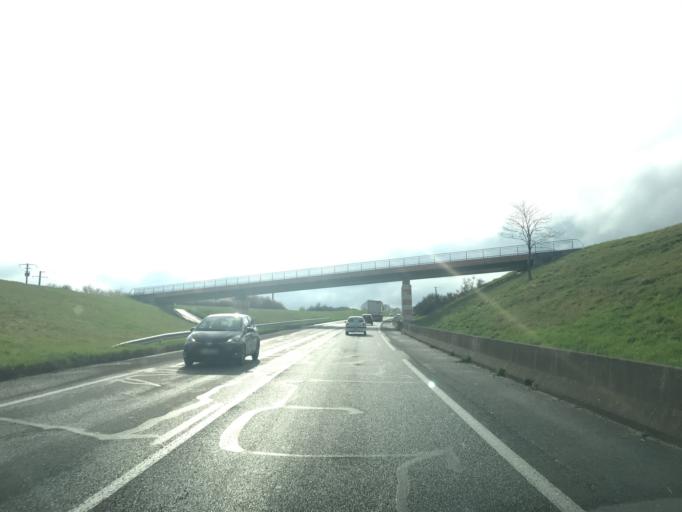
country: FR
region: Centre
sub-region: Departement du Loiret
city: Gien
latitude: 47.7128
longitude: 2.6097
